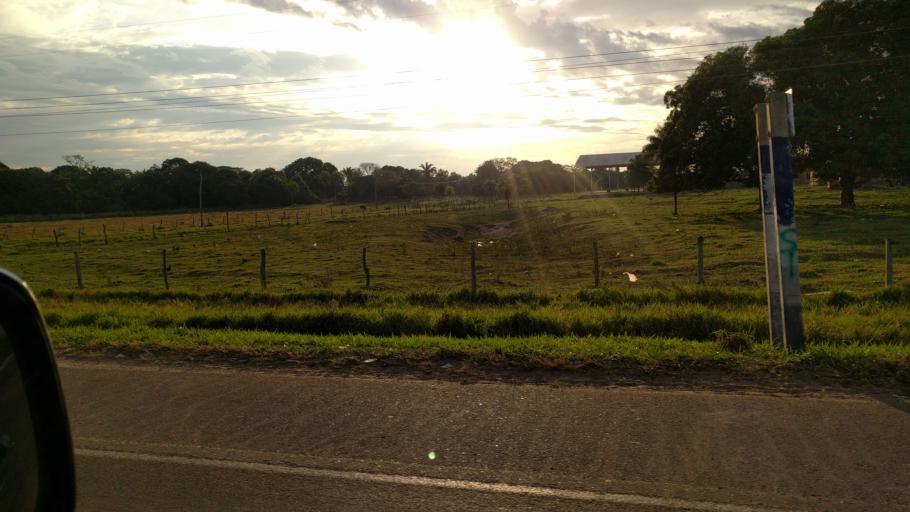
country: BO
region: Santa Cruz
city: Buena Vista
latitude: -17.4091
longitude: -63.6118
